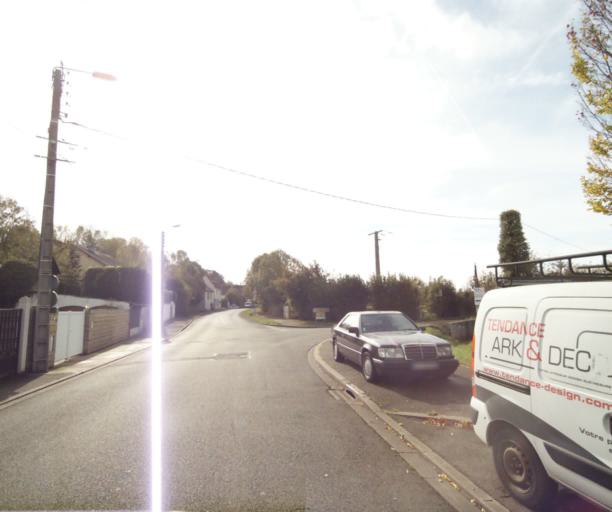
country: FR
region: Centre
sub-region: Departement d'Eure-et-Loir
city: Dreux
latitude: 48.7271
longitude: 1.3620
